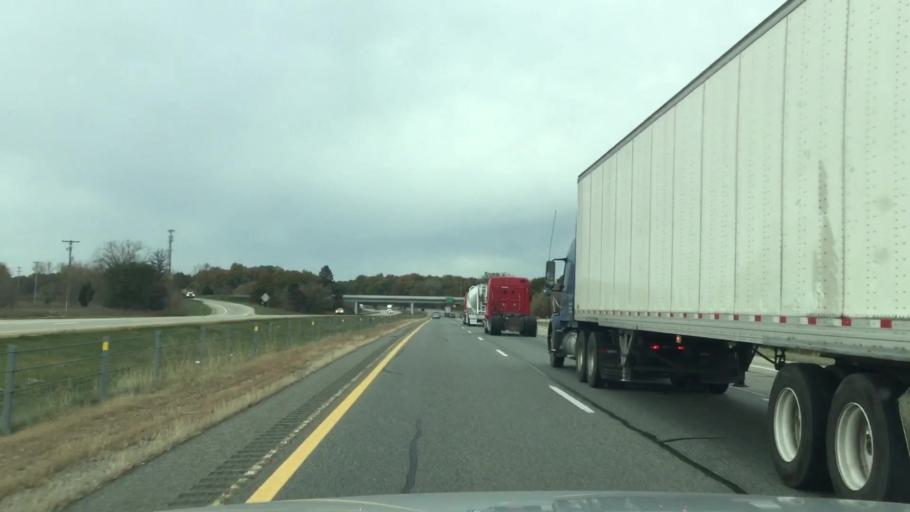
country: US
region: Michigan
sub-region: Jackson County
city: Grass Lake
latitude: 42.2965
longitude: -84.1413
